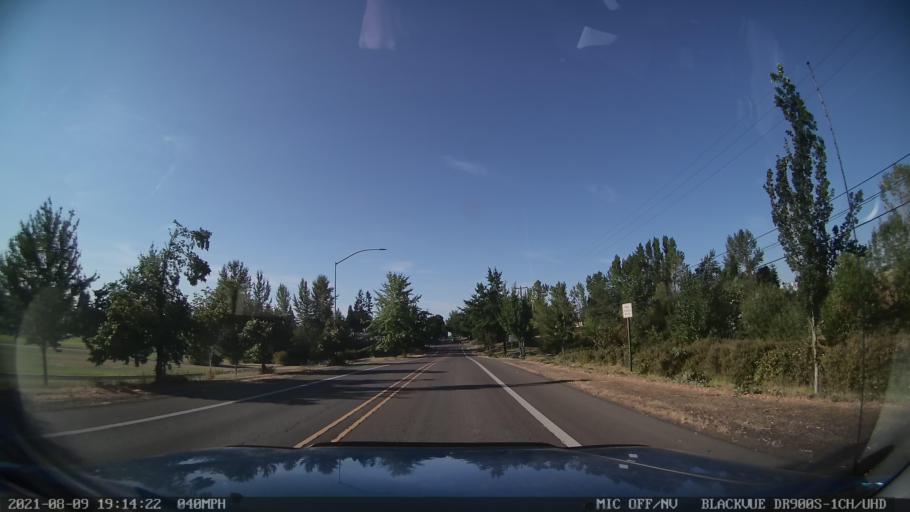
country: US
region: Oregon
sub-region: Marion County
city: Four Corners
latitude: 44.9321
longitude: -122.9917
